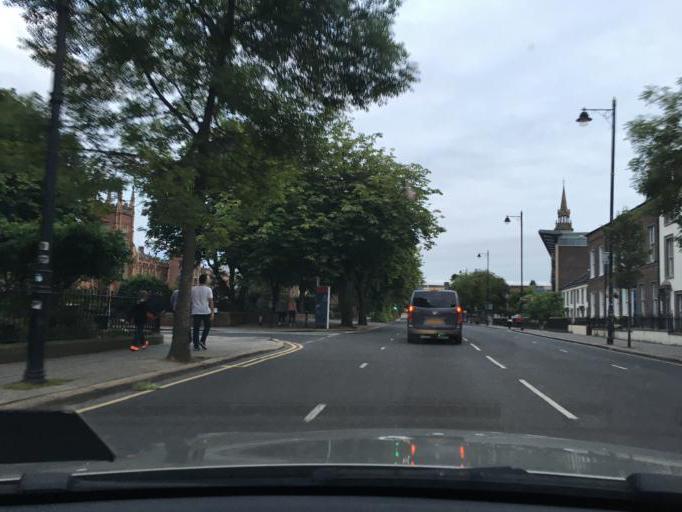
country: GB
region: Northern Ireland
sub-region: City of Belfast
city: Belfast
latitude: 54.5857
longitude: -5.9361
